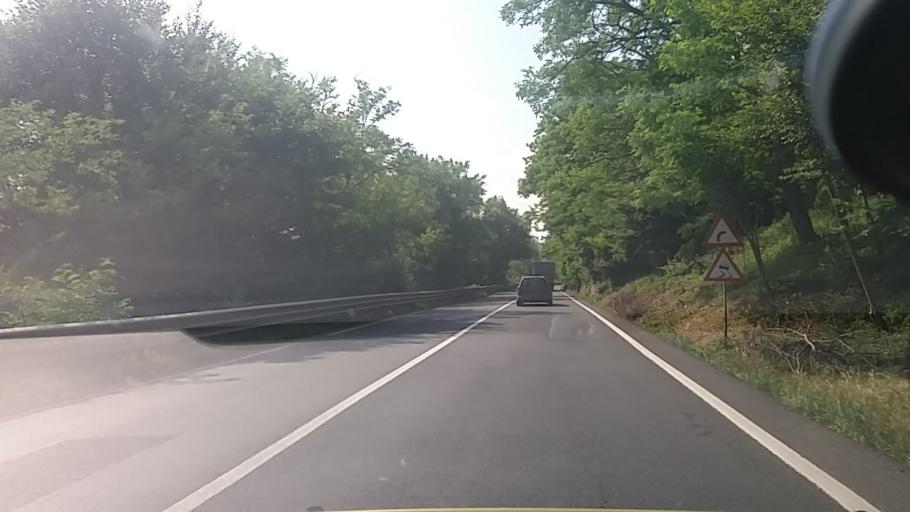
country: RO
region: Arad
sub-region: Comuna Bata
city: Bata
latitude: 46.0368
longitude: 22.0625
